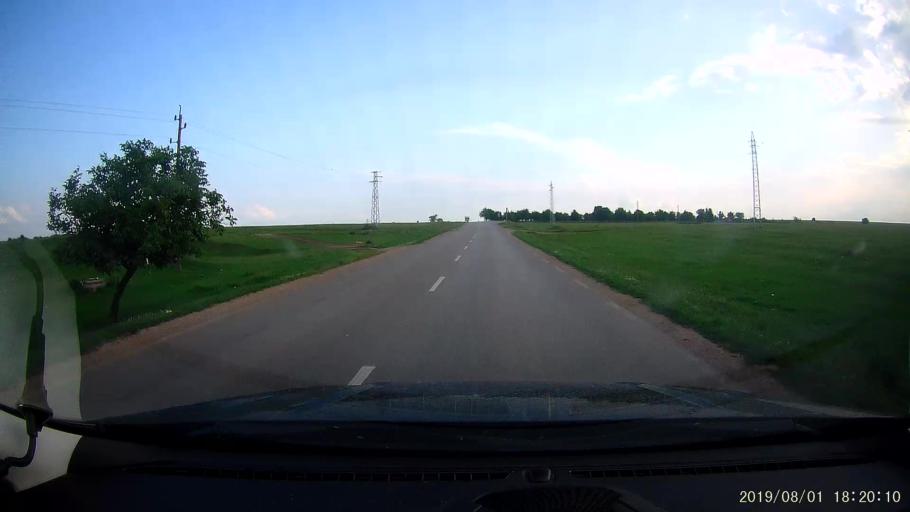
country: BG
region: Shumen
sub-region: Obshtina Kaolinovo
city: Kaolinovo
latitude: 43.6765
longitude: 27.0901
